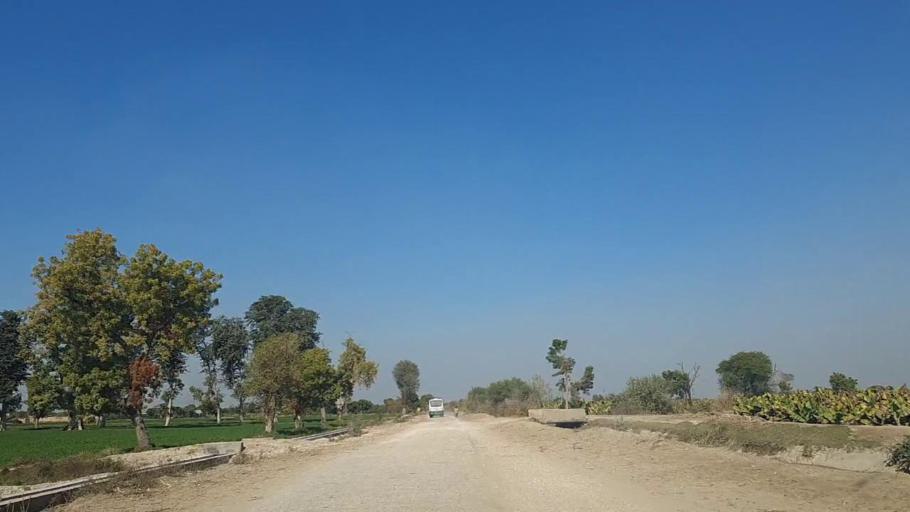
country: PK
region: Sindh
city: Sakrand
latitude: 26.2499
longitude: 68.2207
